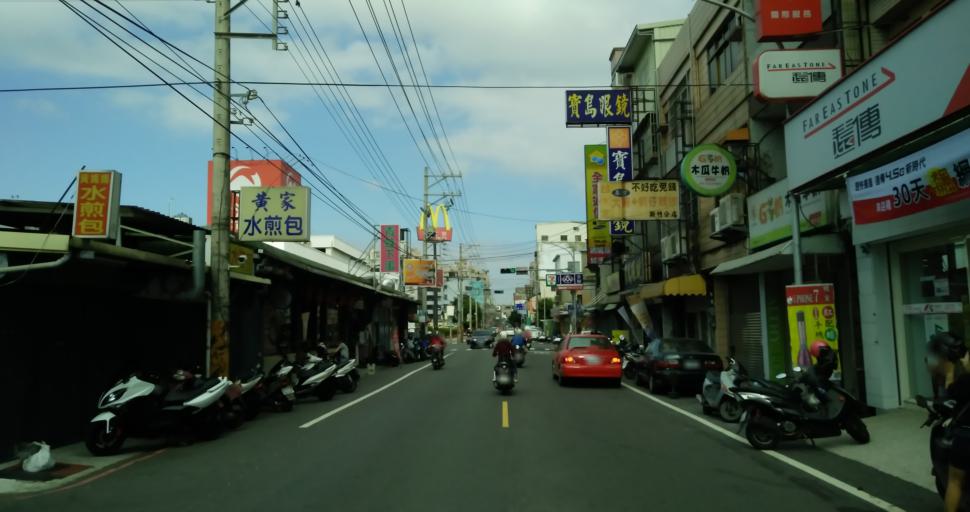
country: TW
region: Taiwan
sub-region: Hsinchu
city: Hsinchu
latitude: 24.8175
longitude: 120.9702
